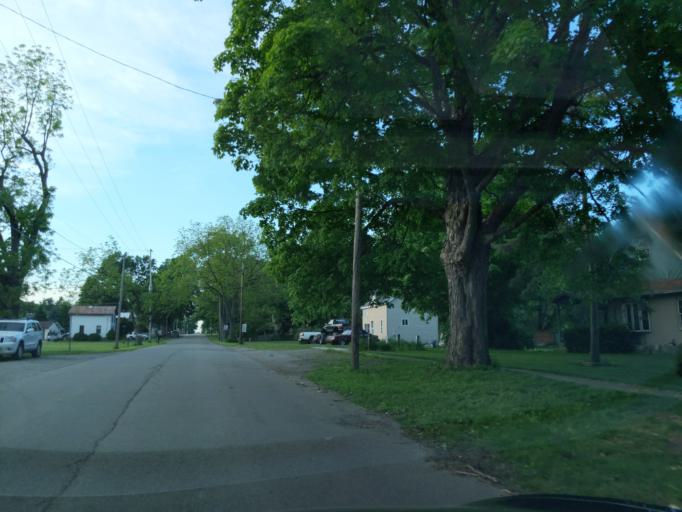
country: US
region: Michigan
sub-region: Ingham County
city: Williamston
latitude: 42.5520
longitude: -84.3029
